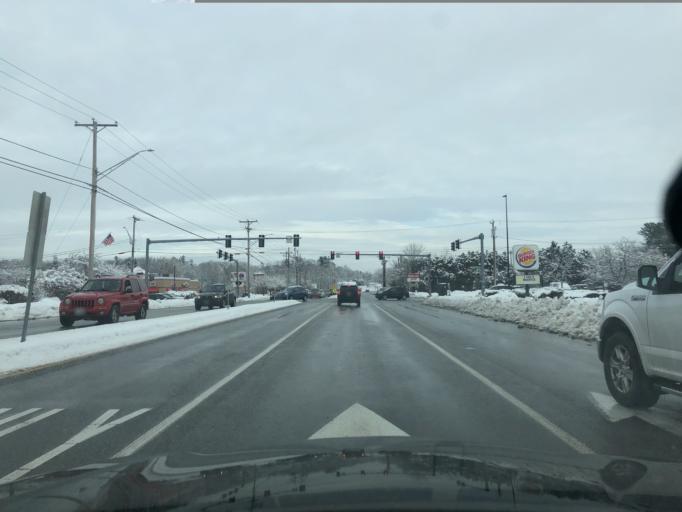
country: US
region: New Hampshire
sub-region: Strafford County
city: Somersworth
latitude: 43.2352
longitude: -70.8814
